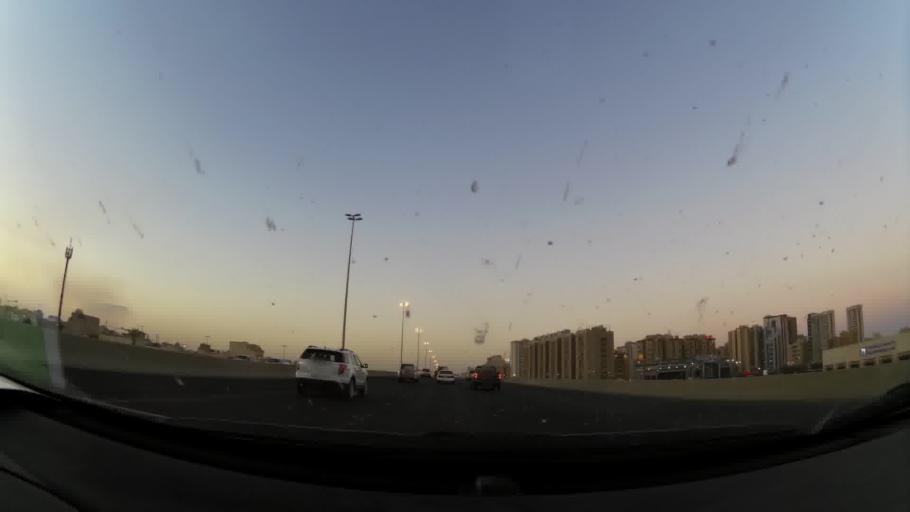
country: KW
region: Al Ahmadi
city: Al Mahbulah
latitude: 29.1348
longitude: 48.1145
